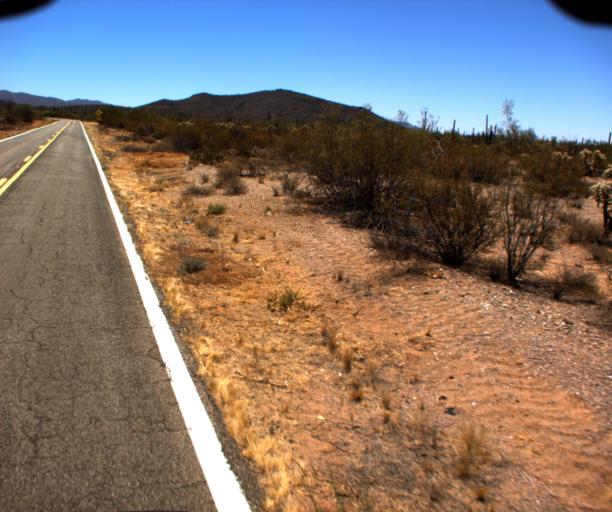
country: US
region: Arizona
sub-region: Pima County
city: Sells
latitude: 32.1794
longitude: -112.2756
